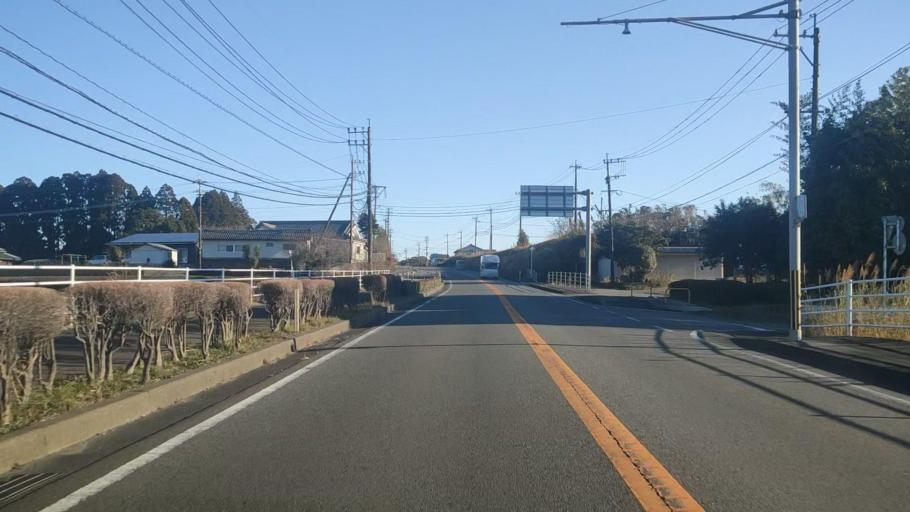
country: JP
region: Miyazaki
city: Takanabe
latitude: 32.3122
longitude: 131.5870
